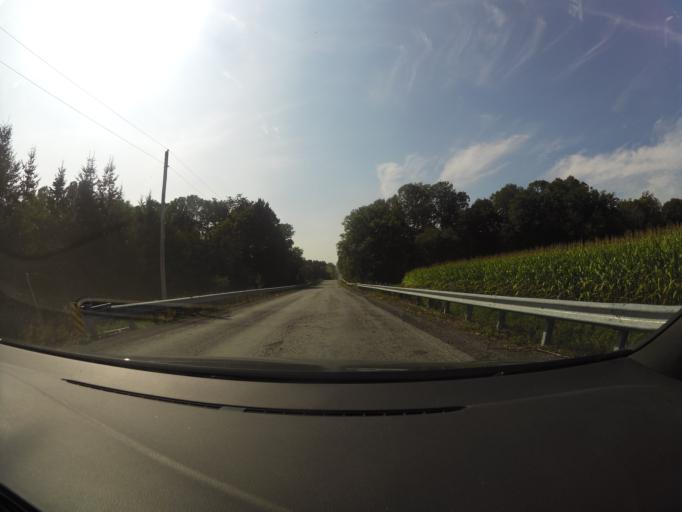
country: CA
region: Ontario
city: Carleton Place
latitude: 45.3100
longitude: -76.1994
